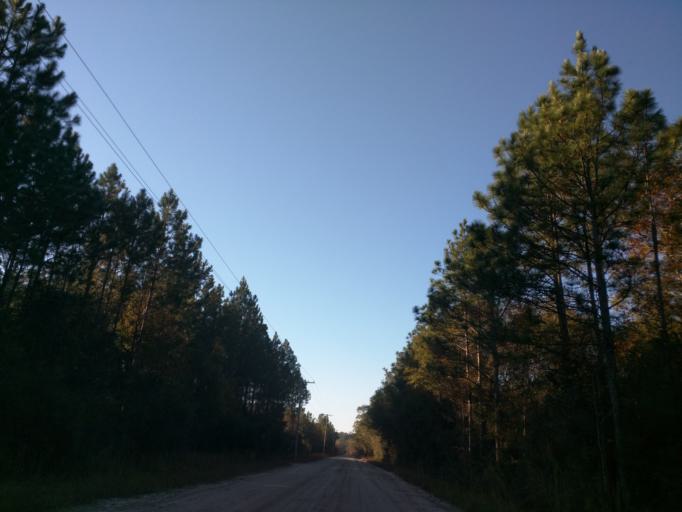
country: US
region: Florida
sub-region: Leon County
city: Woodville
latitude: 30.2510
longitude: -84.1680
